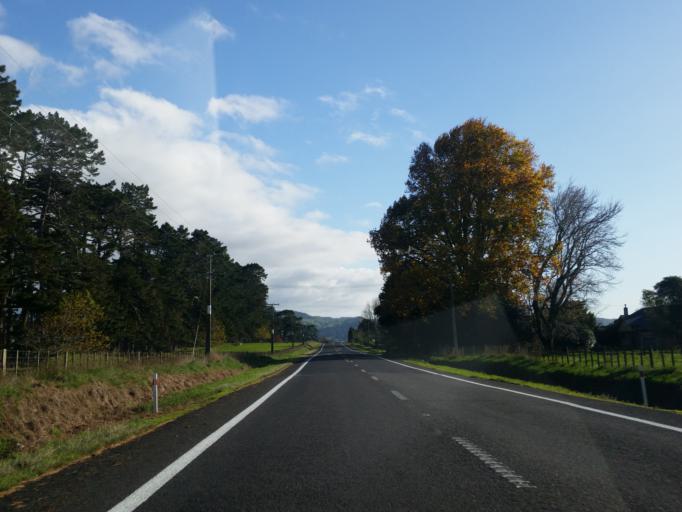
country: NZ
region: Waikato
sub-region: Hauraki District
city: Waihi
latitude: -37.4216
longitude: 175.8682
